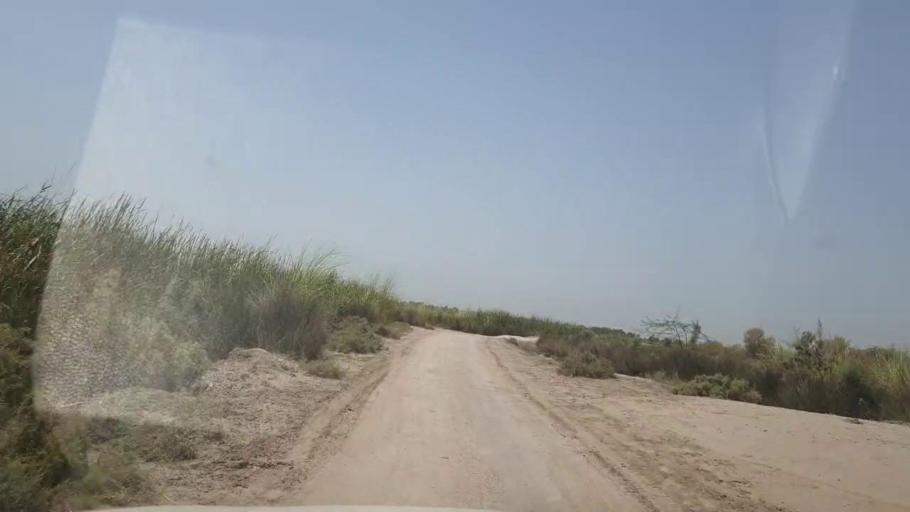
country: PK
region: Sindh
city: Bozdar
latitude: 27.1360
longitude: 68.6176
